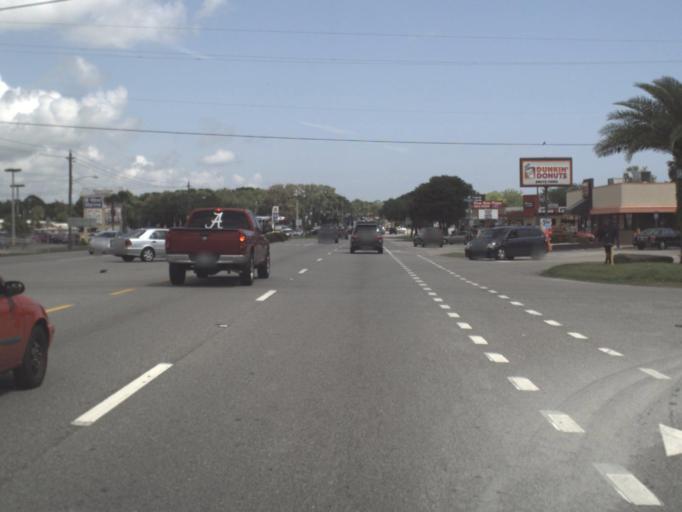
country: US
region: Florida
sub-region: Saint Johns County
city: Saint Augustine
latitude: 29.8785
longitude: -81.3245
